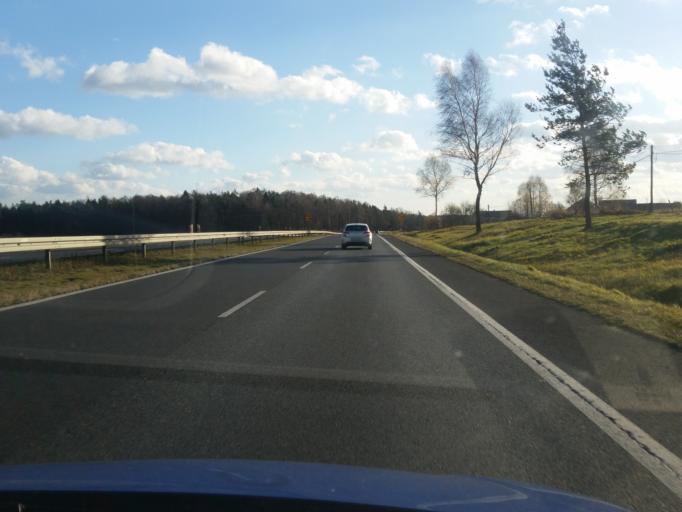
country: PL
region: Silesian Voivodeship
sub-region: Powiat myszkowski
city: Kozieglowy
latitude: 50.5503
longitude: 19.1793
